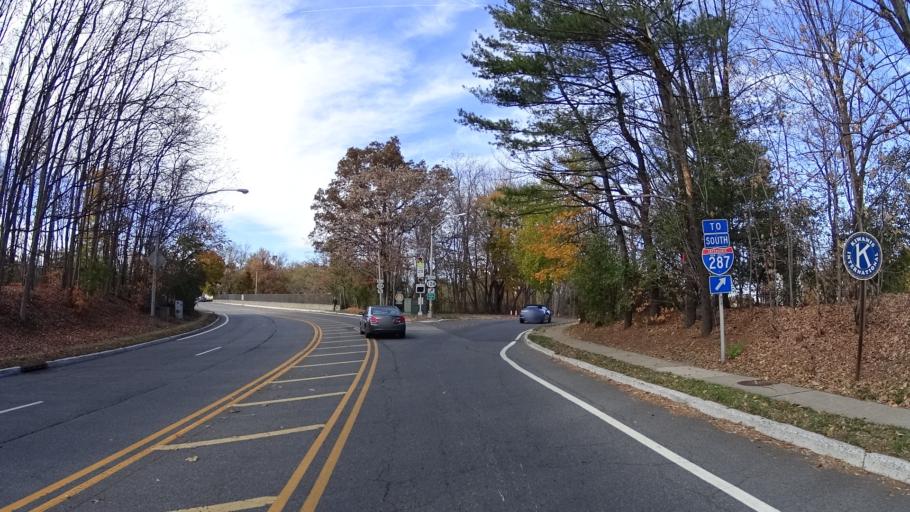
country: US
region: New Jersey
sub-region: Morris County
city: Morristown
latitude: 40.7861
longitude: -74.4684
